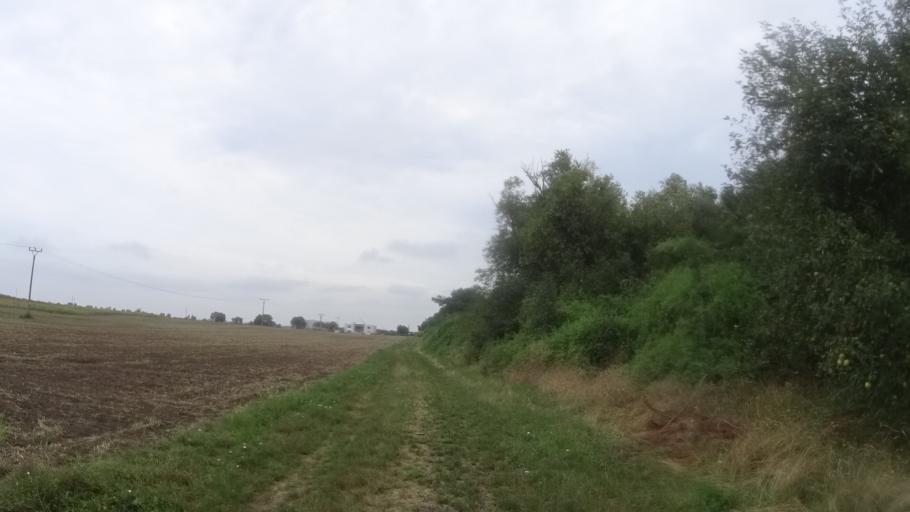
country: SK
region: Nitriansky
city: Komarno
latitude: 47.7627
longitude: 18.0873
